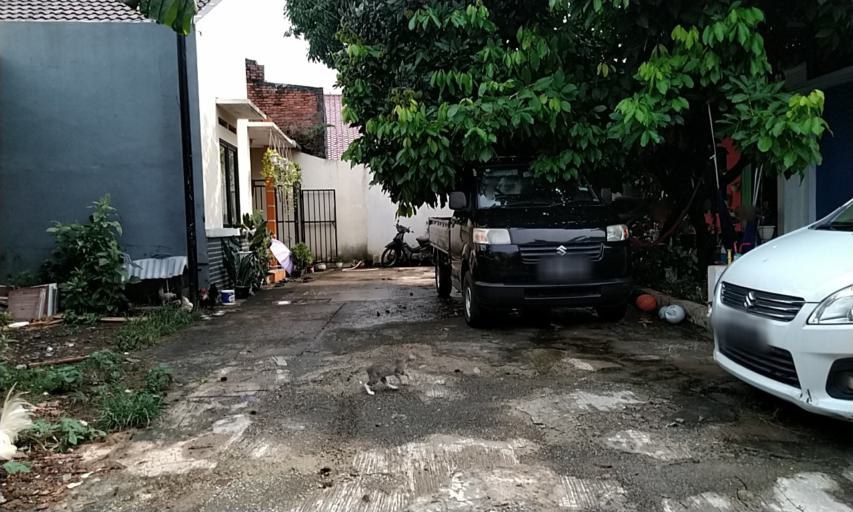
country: ID
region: Banten
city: South Tangerang
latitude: -6.2825
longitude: 106.7621
